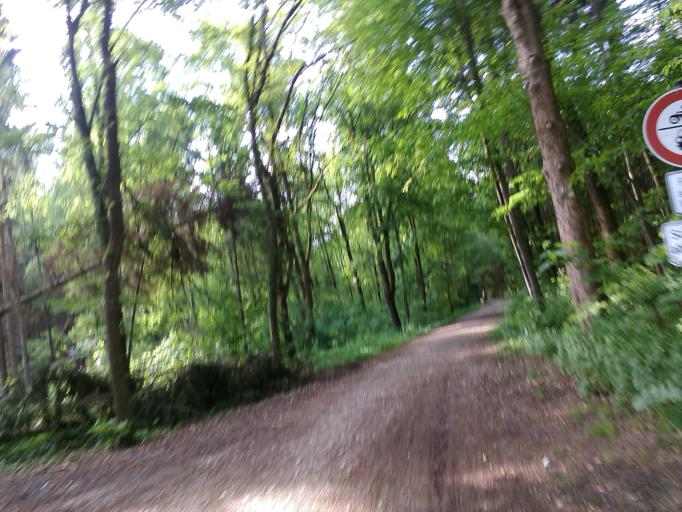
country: DE
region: Bavaria
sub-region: Upper Bavaria
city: Gauting
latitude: 48.0766
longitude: 11.3674
